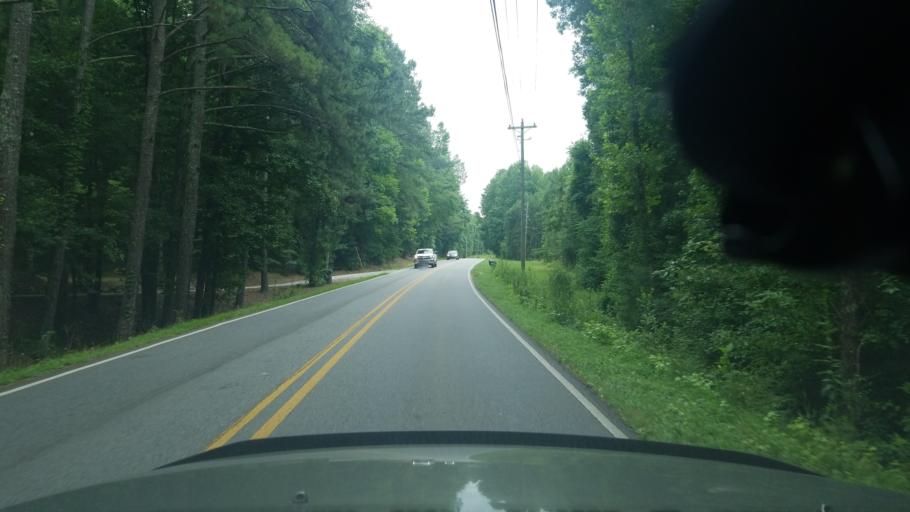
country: US
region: Georgia
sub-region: Forsyth County
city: Cumming
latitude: 34.3054
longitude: -84.1601
